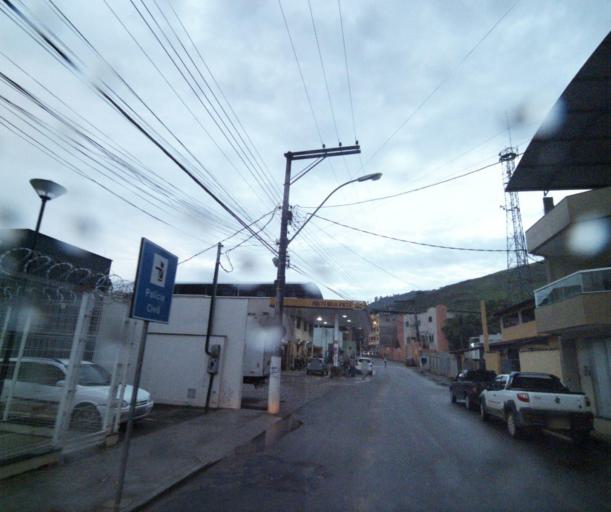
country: BR
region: Espirito Santo
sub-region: Muniz Freire
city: Muniz Freire
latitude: -20.4663
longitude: -41.4144
